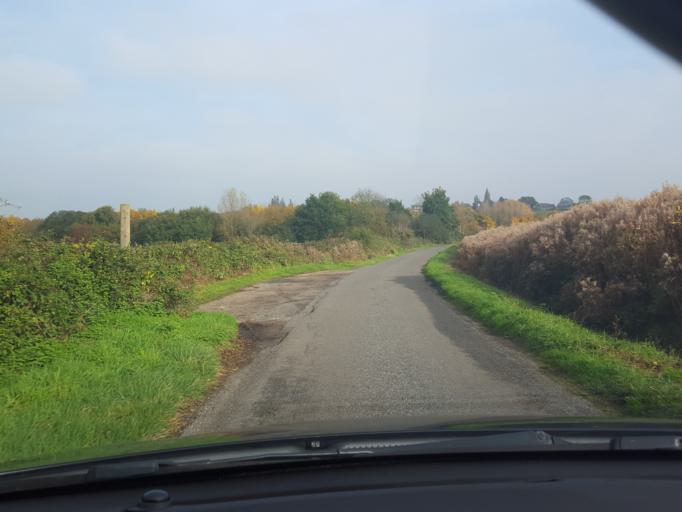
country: GB
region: England
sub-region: Essex
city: Mistley
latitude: 51.9391
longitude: 1.1533
